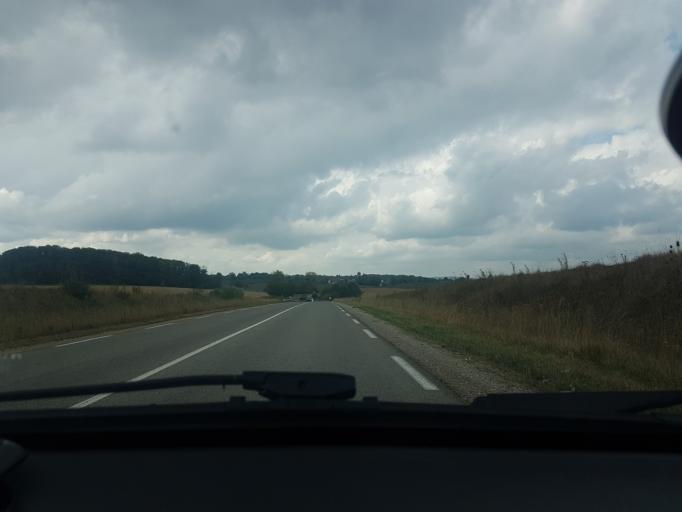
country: FR
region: Franche-Comte
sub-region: Departement de la Haute-Saone
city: Villersexel
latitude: 47.5452
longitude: 6.4758
